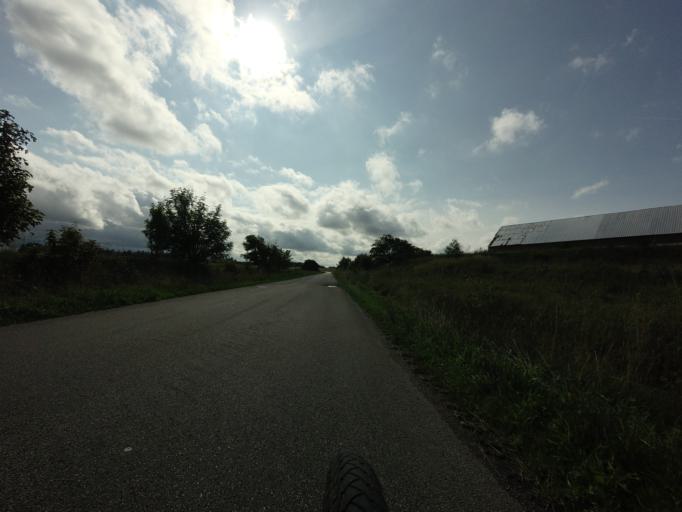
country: DK
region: North Denmark
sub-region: Hjorring Kommune
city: Hirtshals
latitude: 57.5515
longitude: 10.0608
